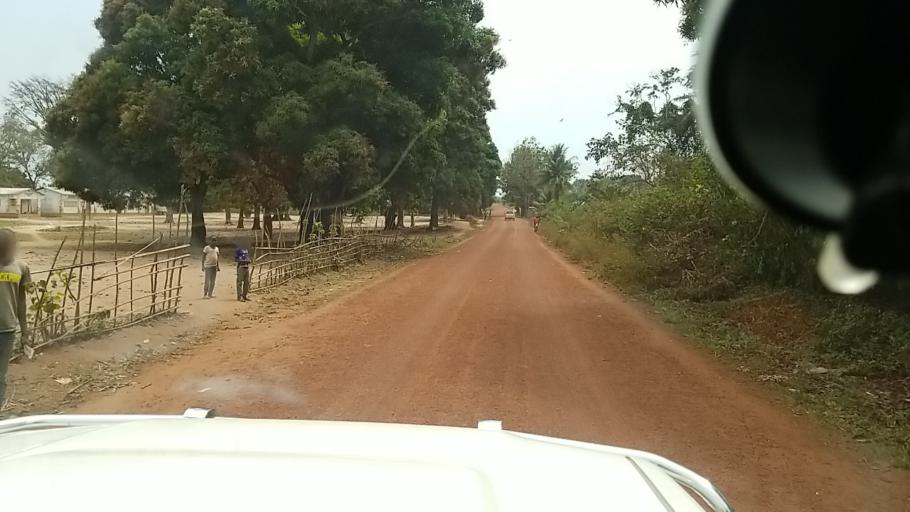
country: CD
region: Equateur
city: Libenge
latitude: 3.7201
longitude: 18.7703
